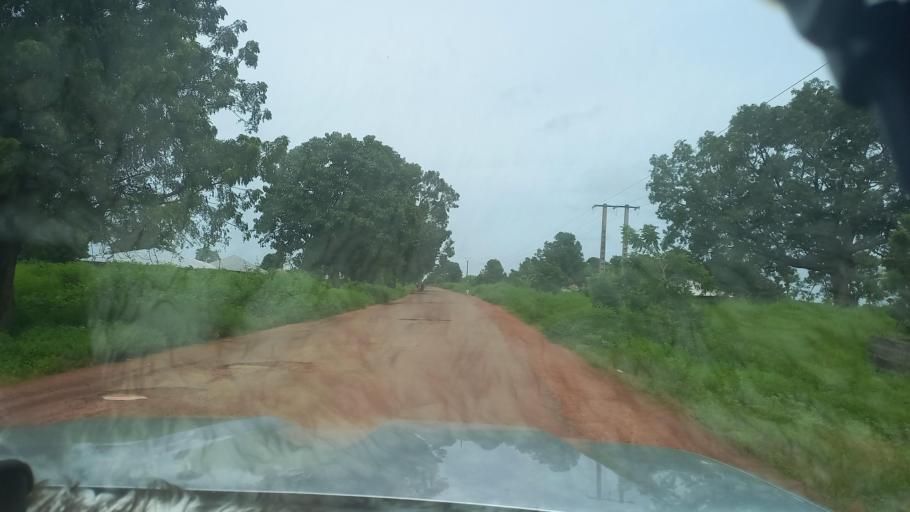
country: SN
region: Kolda
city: Marsassoum
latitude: 12.9160
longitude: -16.0097
